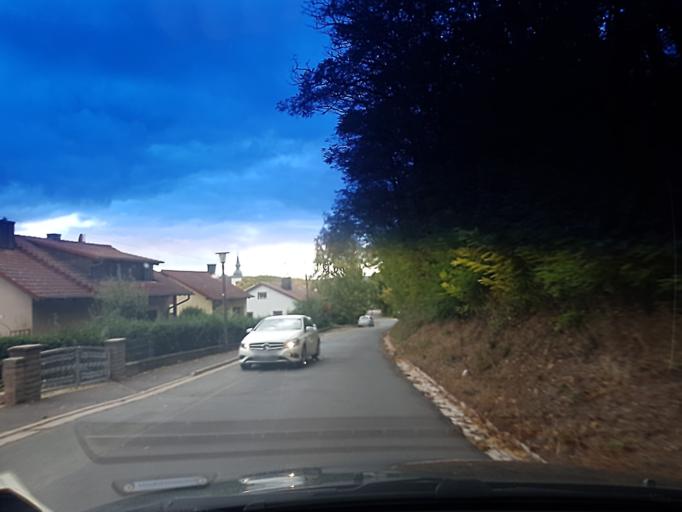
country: DE
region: Bavaria
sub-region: Regierungsbezirk Mittelfranken
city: Burghaslach
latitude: 49.7342
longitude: 10.6046
